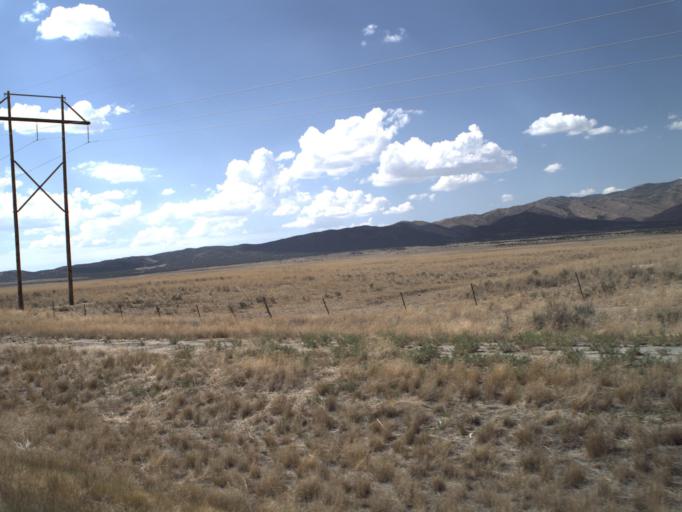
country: US
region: Idaho
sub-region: Power County
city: American Falls
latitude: 41.9666
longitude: -113.0752
